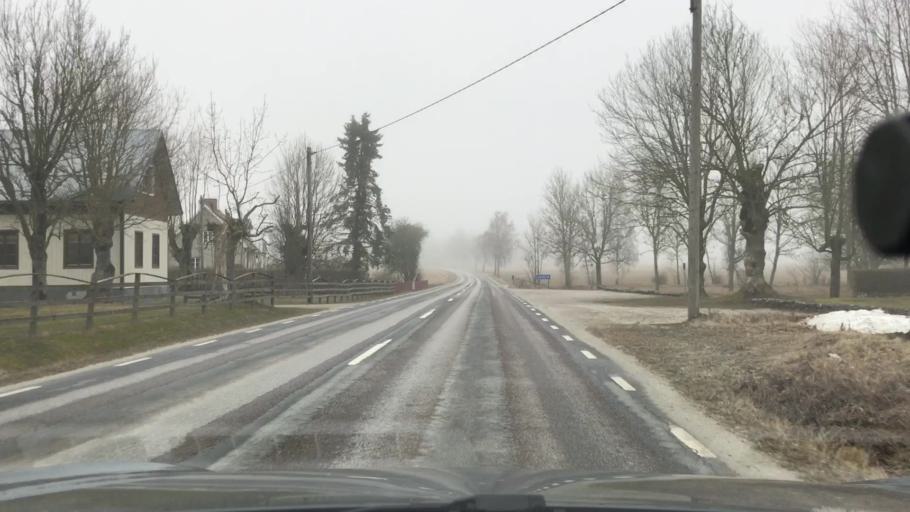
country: SE
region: Gotland
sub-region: Gotland
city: Hemse
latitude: 57.3128
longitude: 18.3823
